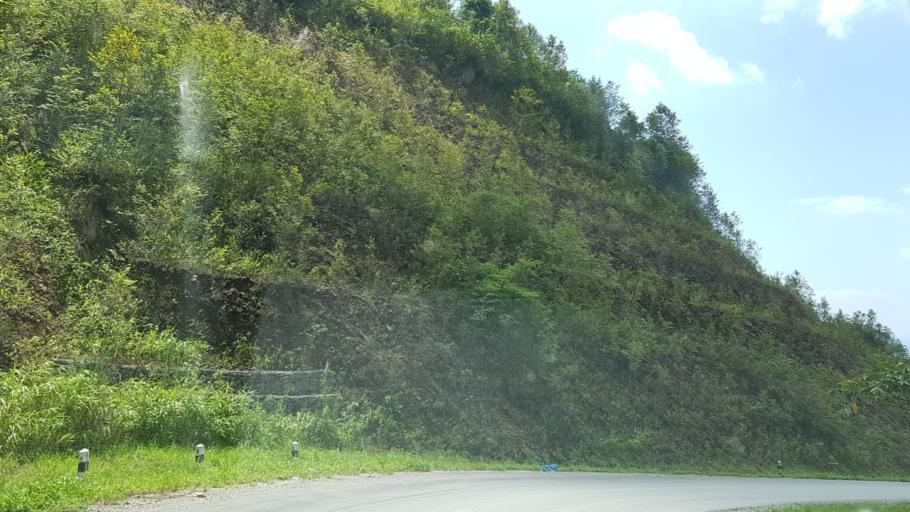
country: LA
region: Vientiane
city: Muang Kasi
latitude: 19.3817
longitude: 102.1544
